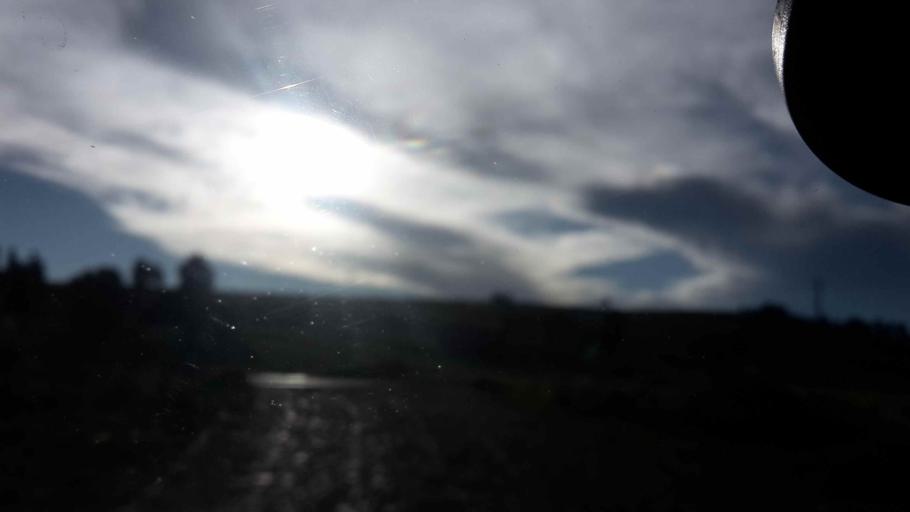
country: BO
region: Cochabamba
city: Arani
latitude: -17.5303
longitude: -65.6596
